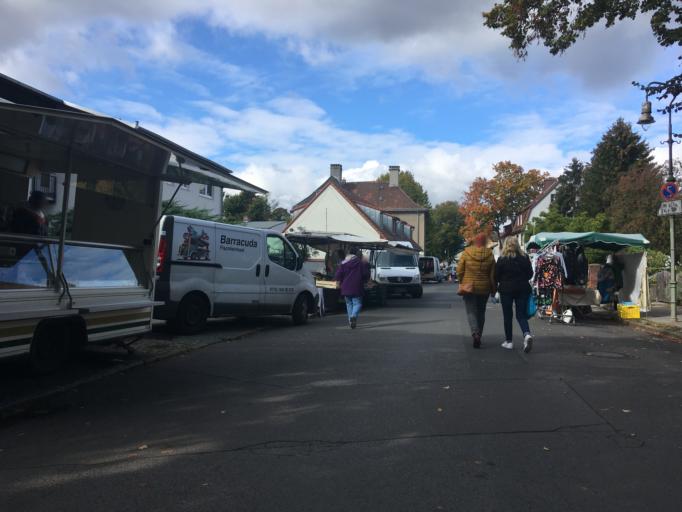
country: DE
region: Berlin
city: Rudow
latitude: 52.4197
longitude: 13.4968
